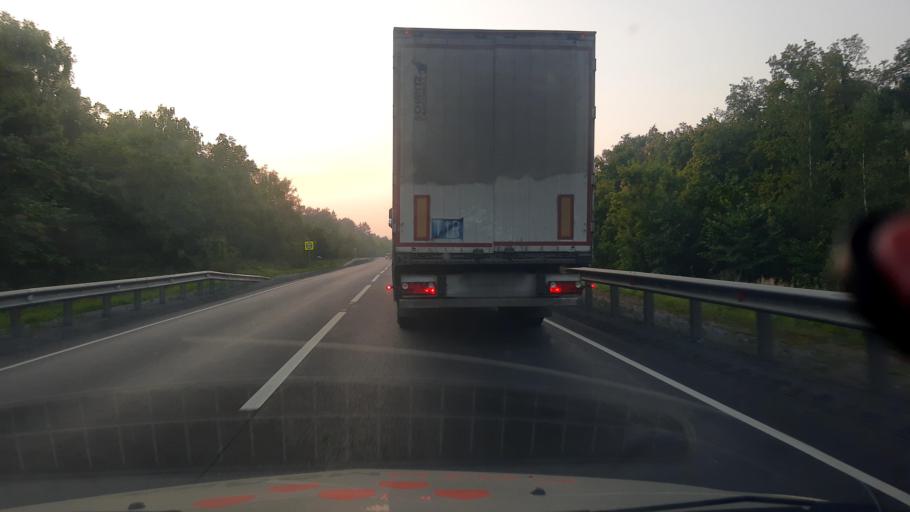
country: RU
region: Bashkortostan
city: Avdon
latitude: 54.8423
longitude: 55.7136
